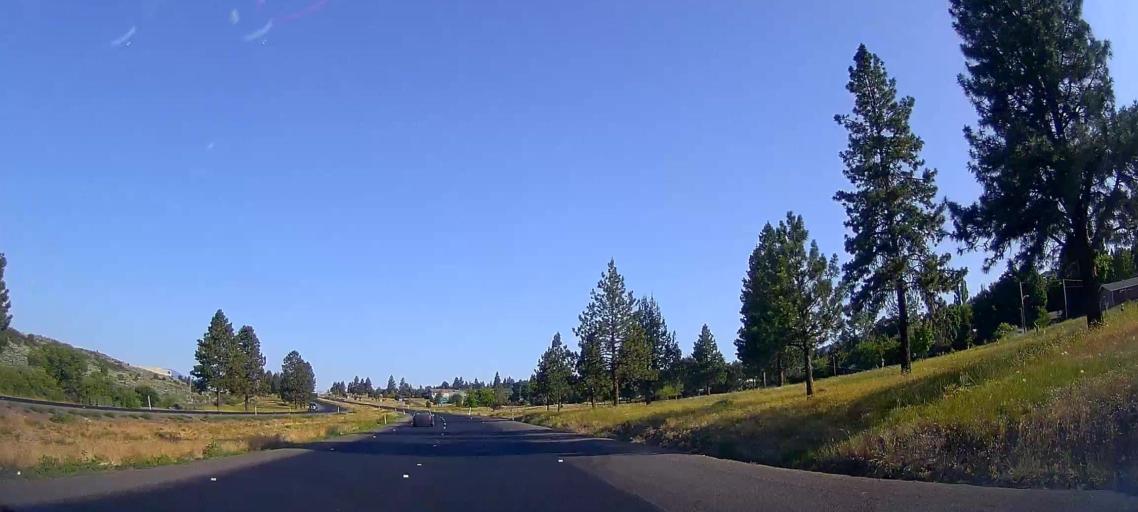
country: US
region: Oregon
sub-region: Klamath County
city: Klamath Falls
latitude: 42.2427
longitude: -121.7824
